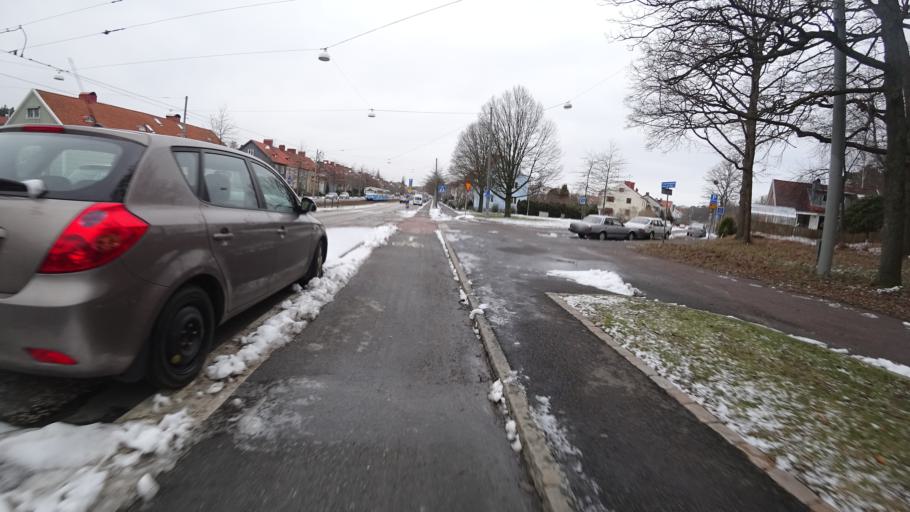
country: SE
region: Vaestra Goetaland
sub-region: Goteborg
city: Majorna
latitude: 57.6806
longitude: 11.9300
